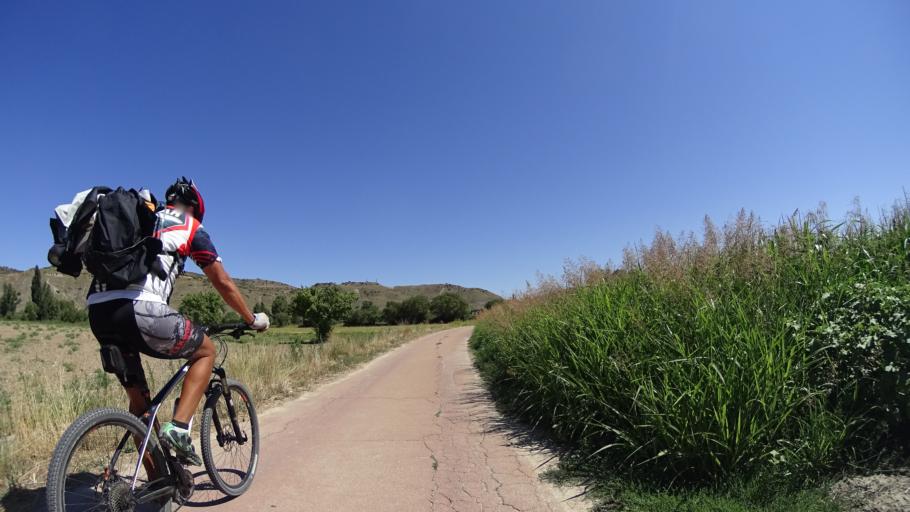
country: ES
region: Madrid
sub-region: Provincia de Madrid
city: Carabana
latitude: 40.2413
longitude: -3.2509
